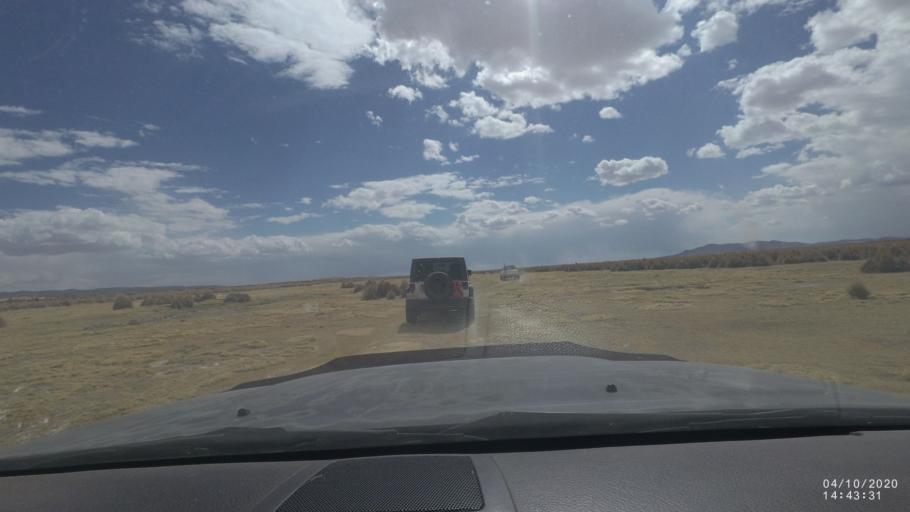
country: BO
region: Oruro
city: Poopo
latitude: -18.6866
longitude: -67.4933
